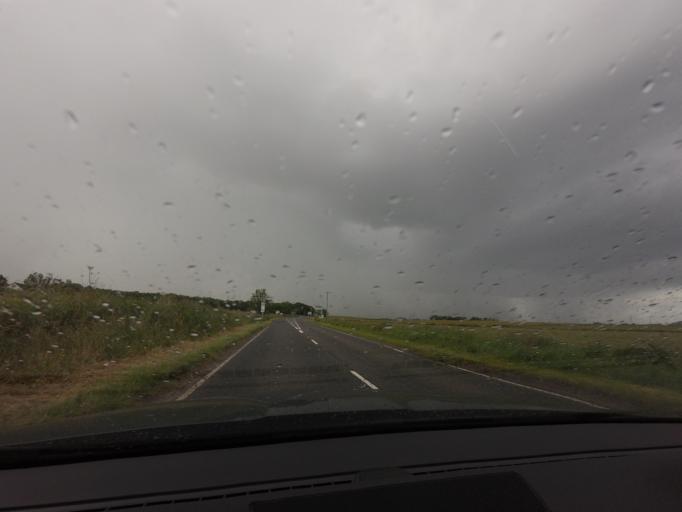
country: GB
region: Scotland
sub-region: Moray
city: Buckie
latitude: 57.6607
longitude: -2.9657
